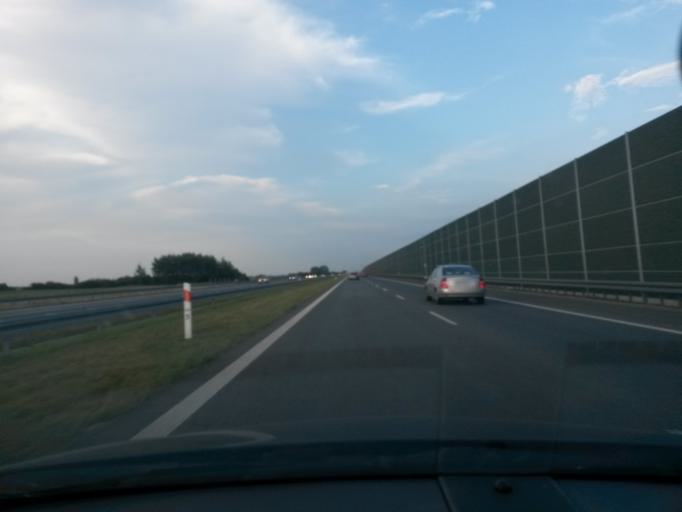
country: PL
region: Masovian Voivodeship
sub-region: Powiat warszawski zachodni
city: Bieniewice
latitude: 52.1375
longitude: 20.5746
